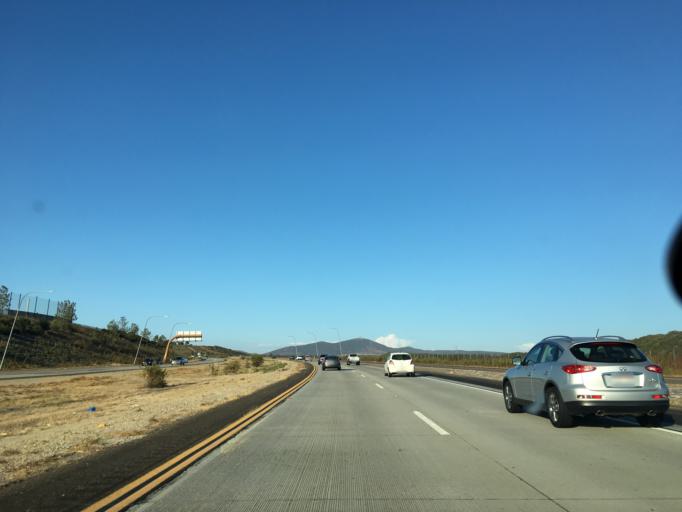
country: US
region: California
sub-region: San Diego County
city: Fairbanks Ranch
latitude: 32.9533
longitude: -117.1906
